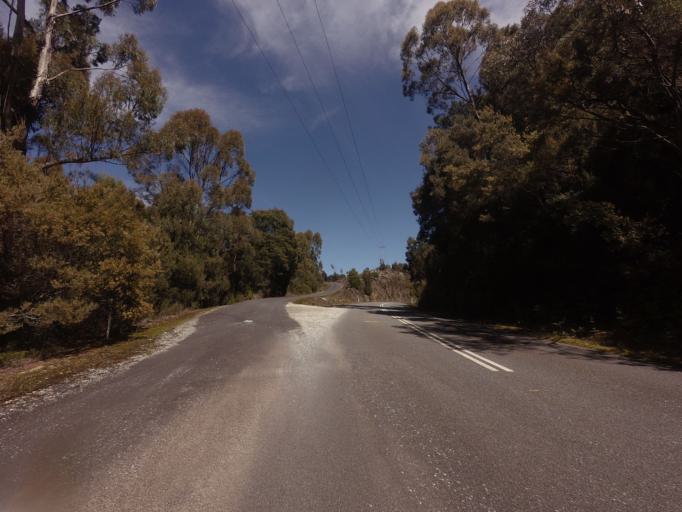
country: AU
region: Tasmania
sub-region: West Coast
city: Queenstown
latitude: -42.7815
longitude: 146.0333
